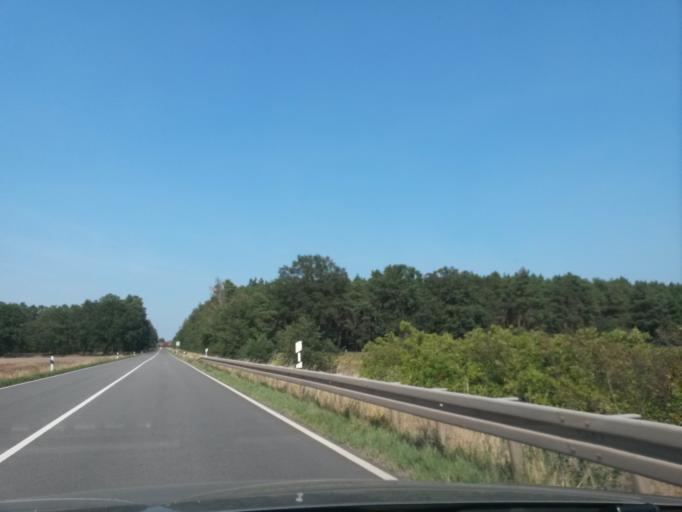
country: DE
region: Saxony-Anhalt
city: Jerichow
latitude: 52.5259
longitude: 12.0159
